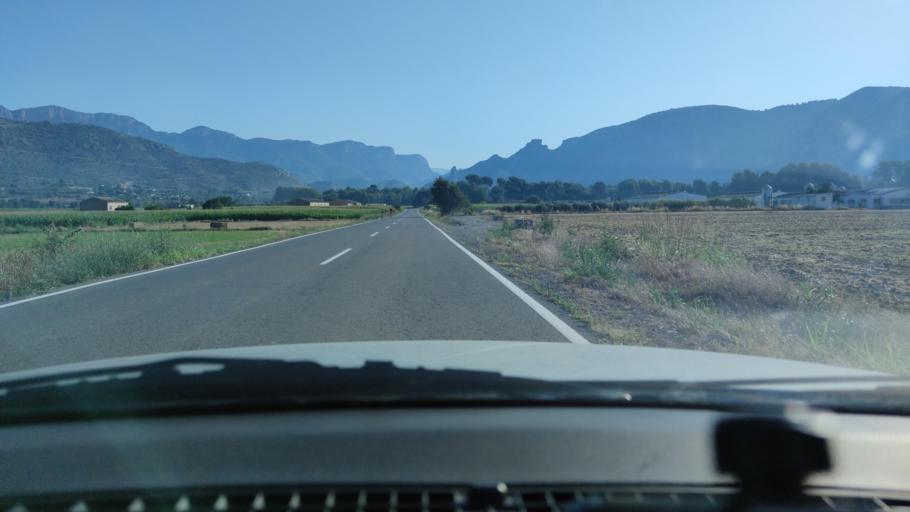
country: ES
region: Catalonia
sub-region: Provincia de Lleida
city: Camarasa
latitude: 41.8516
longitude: 0.8283
